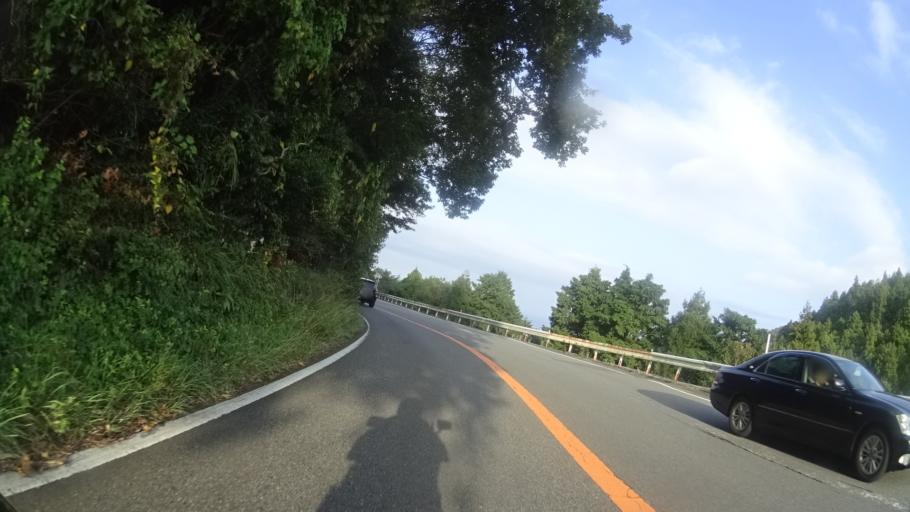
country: JP
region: Oita
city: Beppu
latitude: 33.2849
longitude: 131.4570
